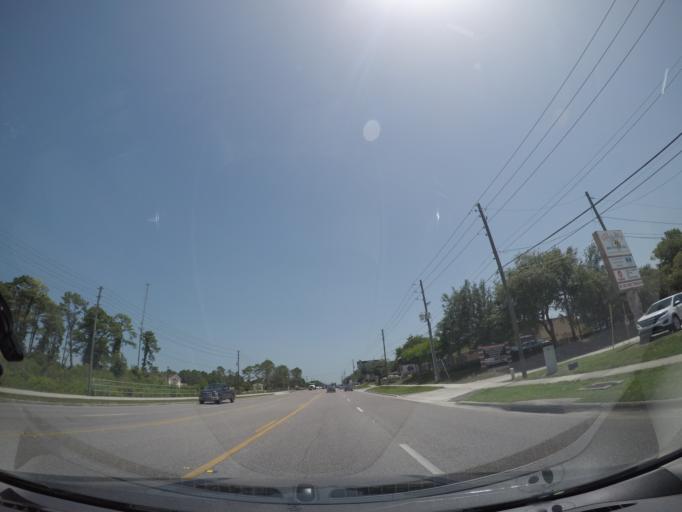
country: US
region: Florida
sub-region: Orange County
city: Apopka
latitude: 28.7019
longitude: -81.5091
